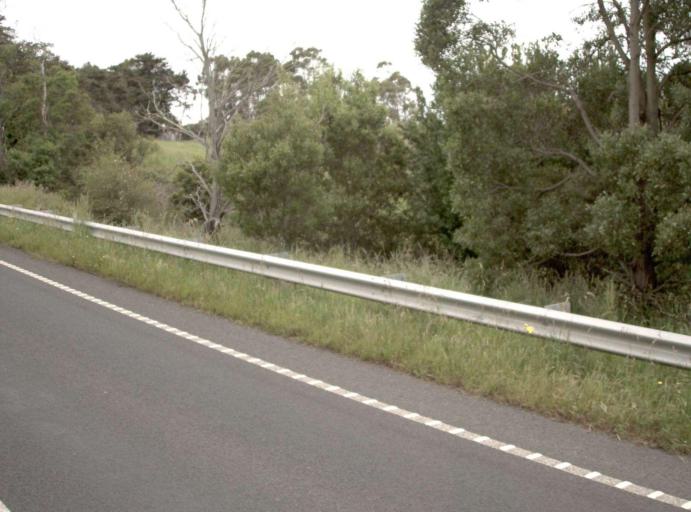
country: AU
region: Victoria
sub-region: Bass Coast
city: North Wonthaggi
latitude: -38.4191
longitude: 145.7883
